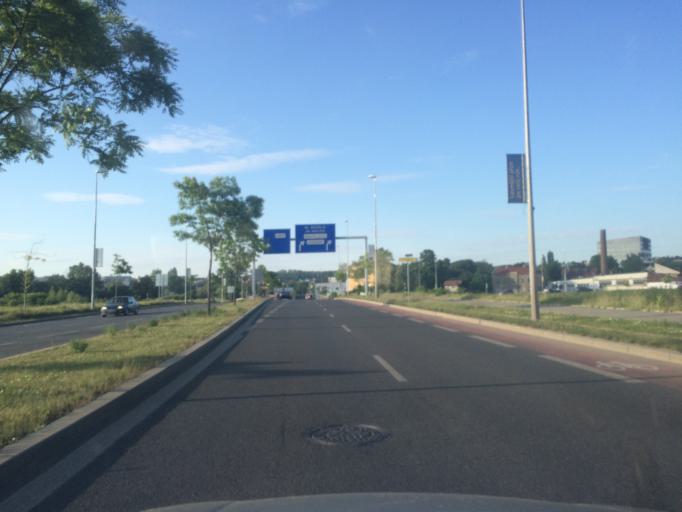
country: CZ
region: Praha
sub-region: Praha 8
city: Liben
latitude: 50.0989
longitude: 14.4654
